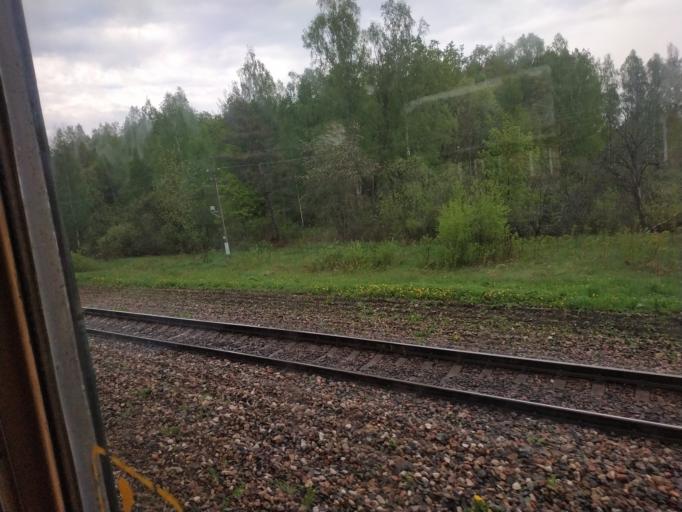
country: RU
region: Kaluga
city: Baryatino
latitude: 54.3517
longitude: 34.3303
